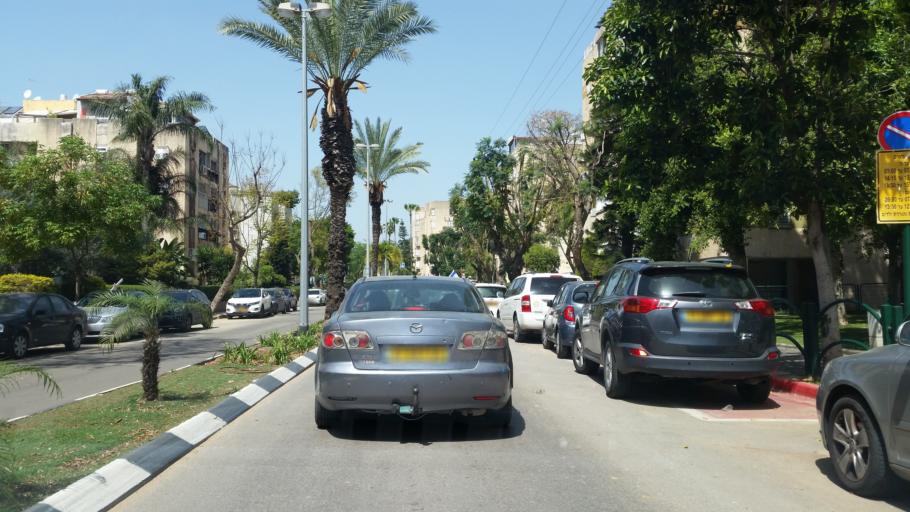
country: IL
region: Central District
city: Ra'anana
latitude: 32.1809
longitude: 34.8818
